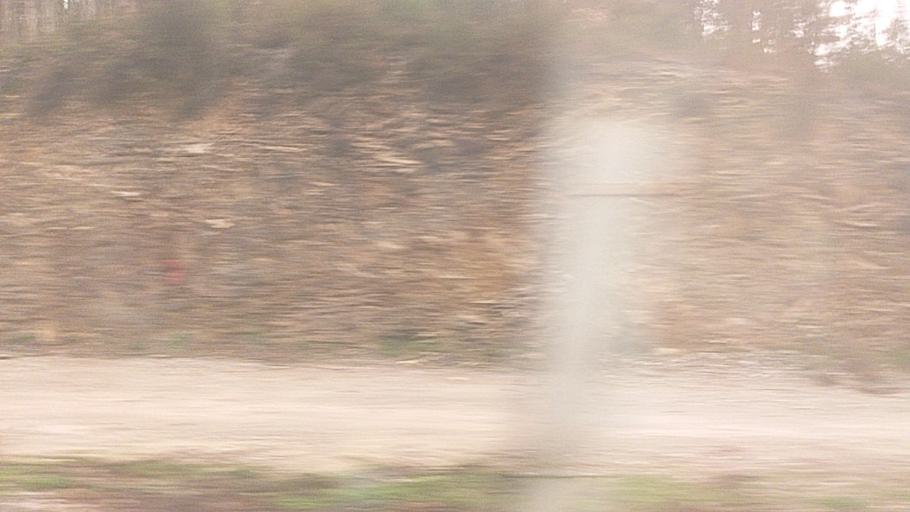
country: PT
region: Viseu
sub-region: Mortagua
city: Mortagua
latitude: 40.4058
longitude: -8.3217
